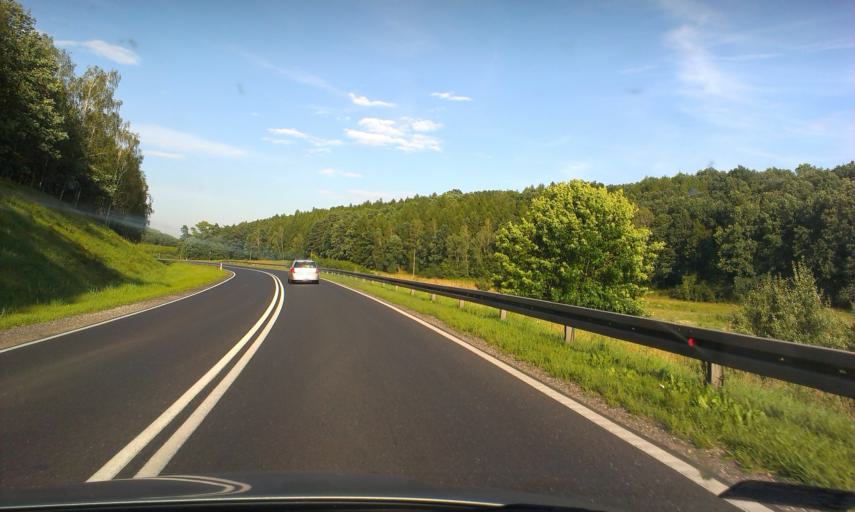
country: PL
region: Kujawsko-Pomorskie
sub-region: Powiat bydgoski
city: Sicienko
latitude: 53.1599
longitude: 17.7965
